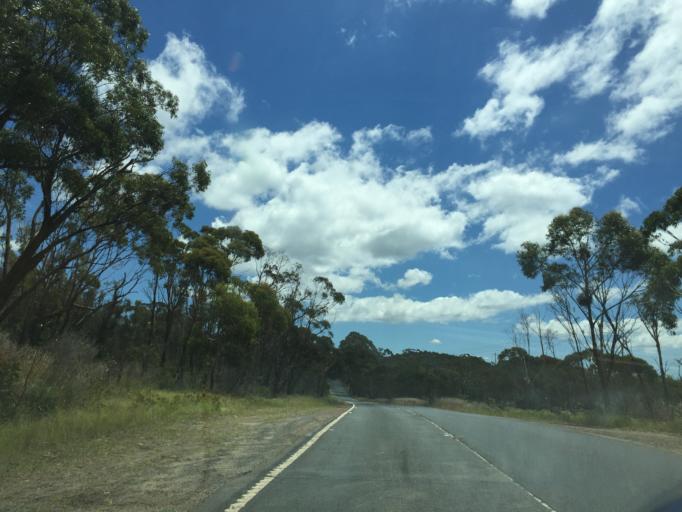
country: AU
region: New South Wales
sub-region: Blue Mountains Municipality
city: Blackheath
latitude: -33.5384
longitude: 150.3285
